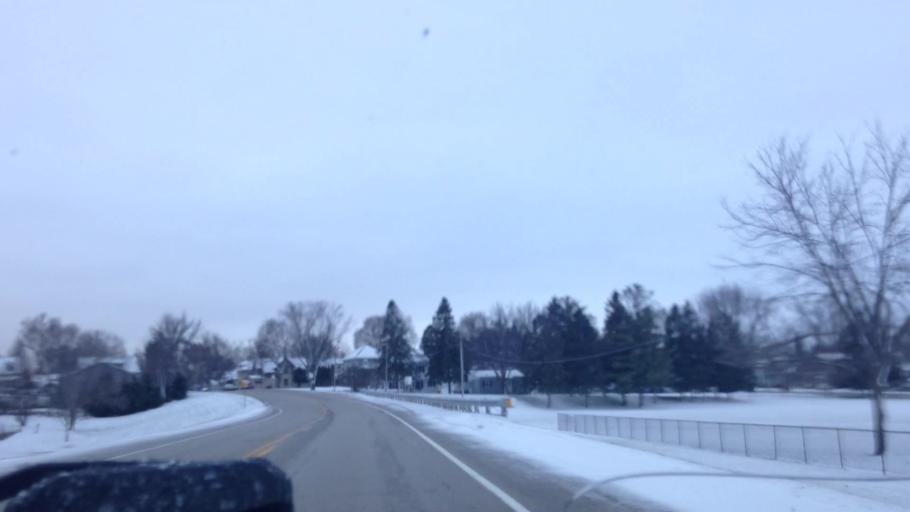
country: US
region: Wisconsin
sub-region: Dodge County
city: Horicon
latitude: 43.4555
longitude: -88.6225
